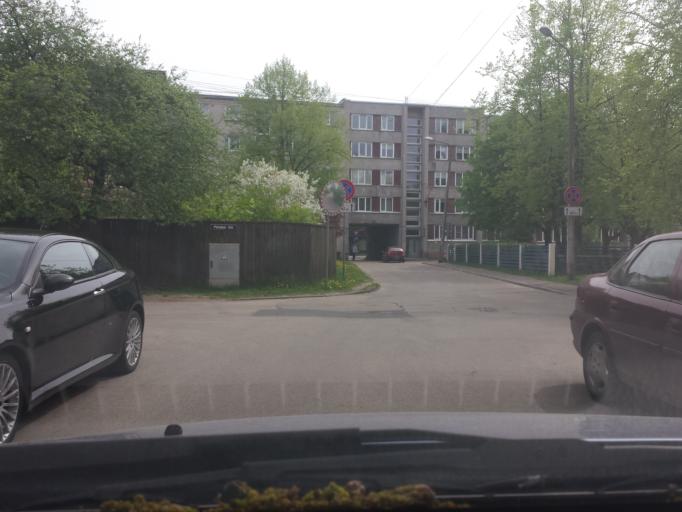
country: LV
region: Riga
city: Jaunciems
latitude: 56.9777
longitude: 24.1781
